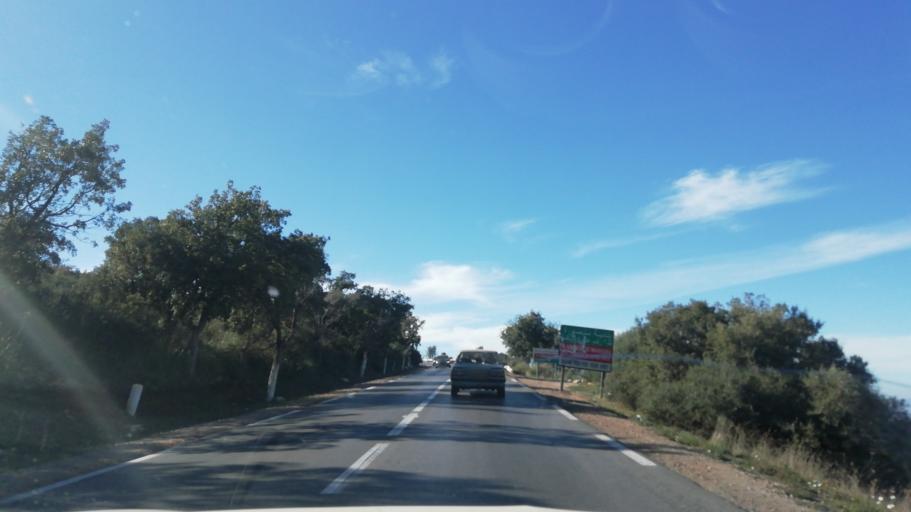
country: DZ
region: Tlemcen
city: Mansoura
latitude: 34.8480
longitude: -1.3606
